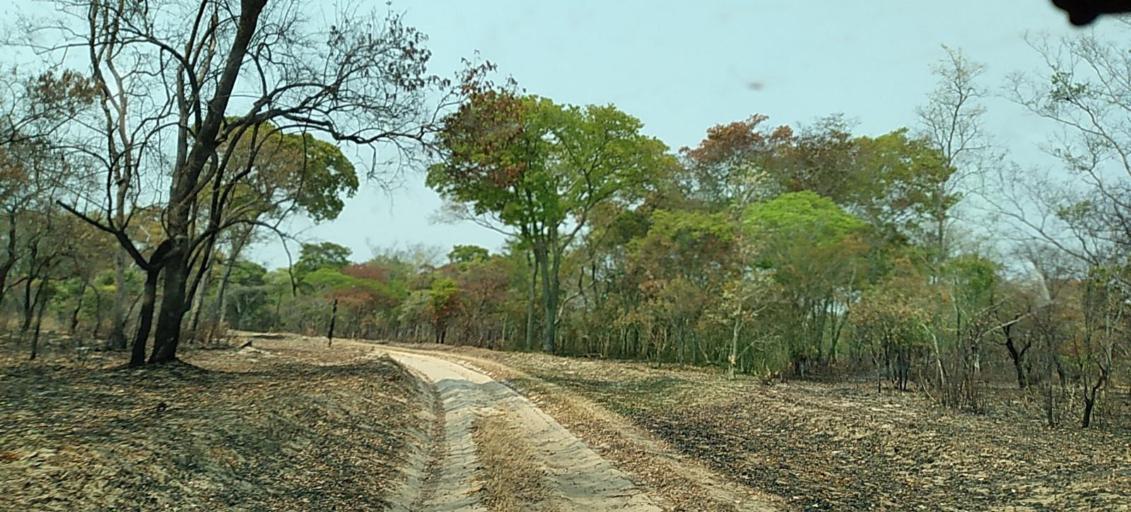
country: ZM
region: North-Western
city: Zambezi
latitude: -13.9370
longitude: 23.2223
